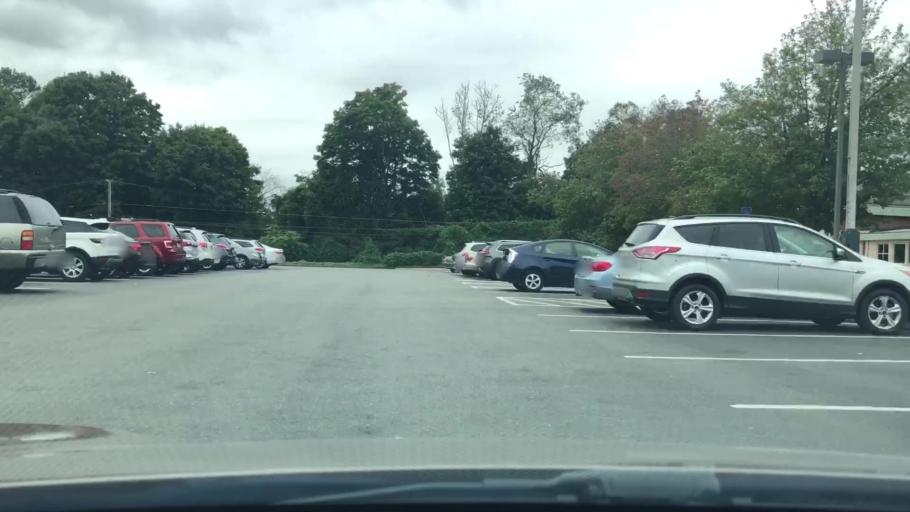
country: US
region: Connecticut
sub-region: Fairfield County
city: Darien
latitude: 41.1157
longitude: -73.4540
